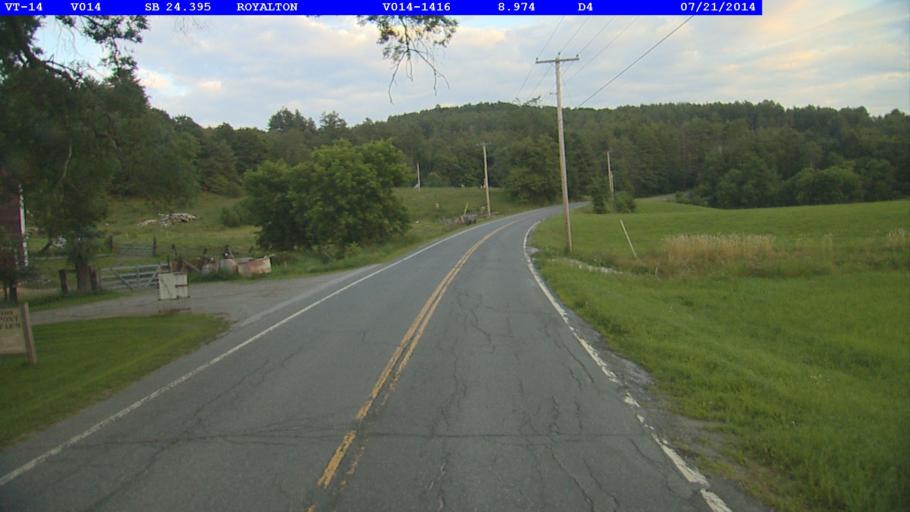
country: US
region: Vermont
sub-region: Orange County
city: Randolph
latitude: 43.8613
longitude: -72.5808
